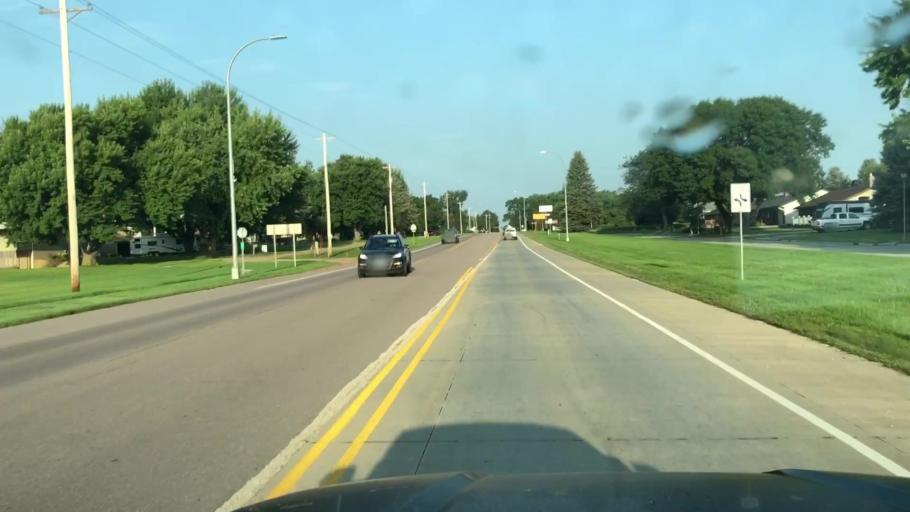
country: US
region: Iowa
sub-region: O'Brien County
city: Sheldon
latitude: 43.1861
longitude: -95.8353
